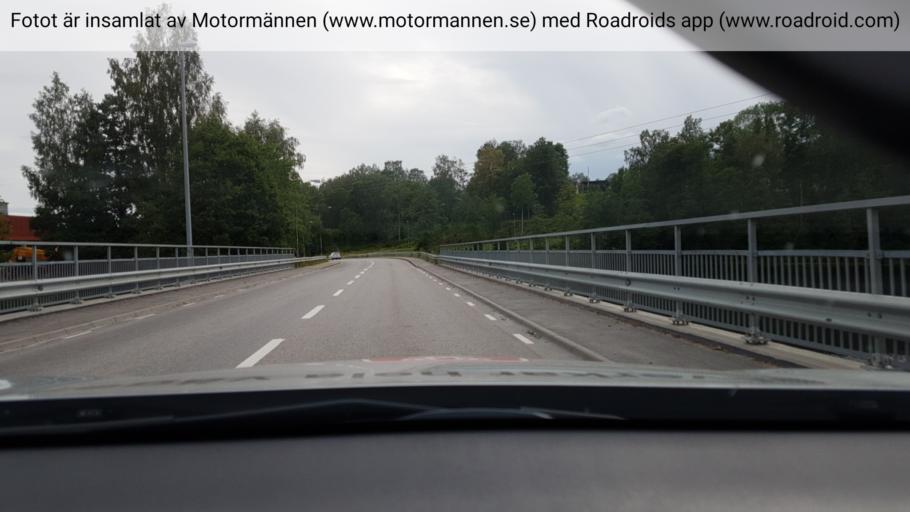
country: SE
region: Vaestra Goetaland
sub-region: Bengtsfors Kommun
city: Billingsfors
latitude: 58.9896
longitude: 12.2552
